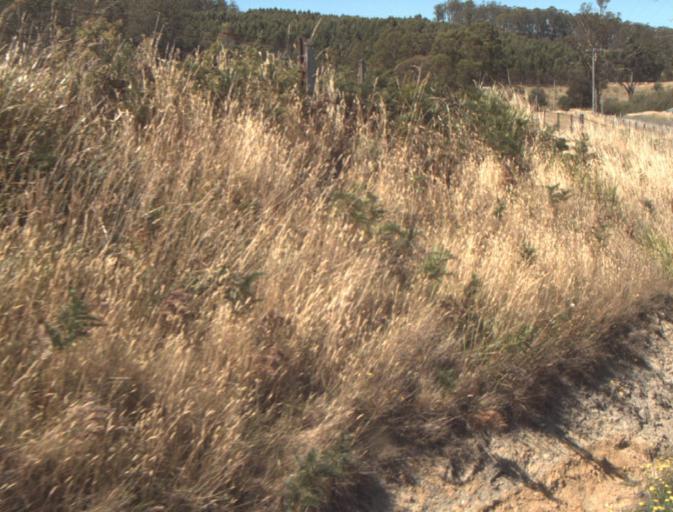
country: AU
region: Tasmania
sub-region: Launceston
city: Newstead
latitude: -41.3461
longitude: 147.3028
